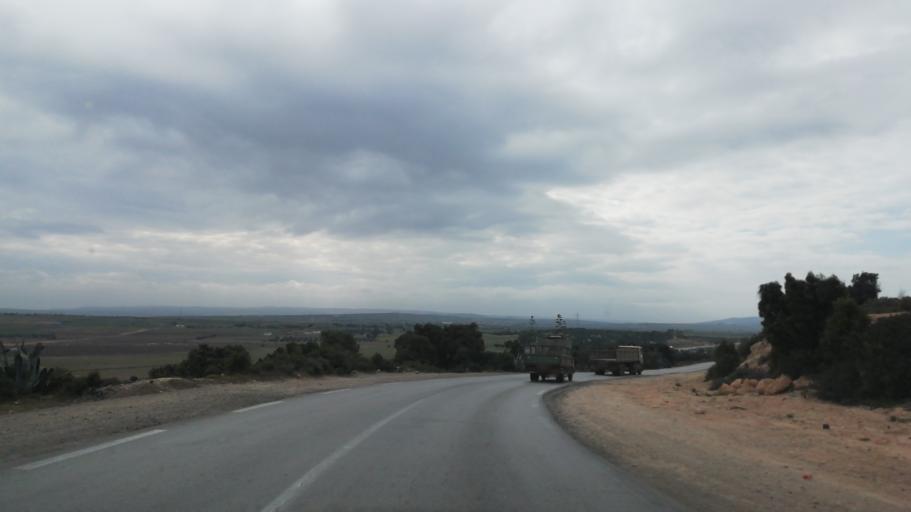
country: DZ
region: Oran
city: Ain el Bya
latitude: 35.7187
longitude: -0.3575
